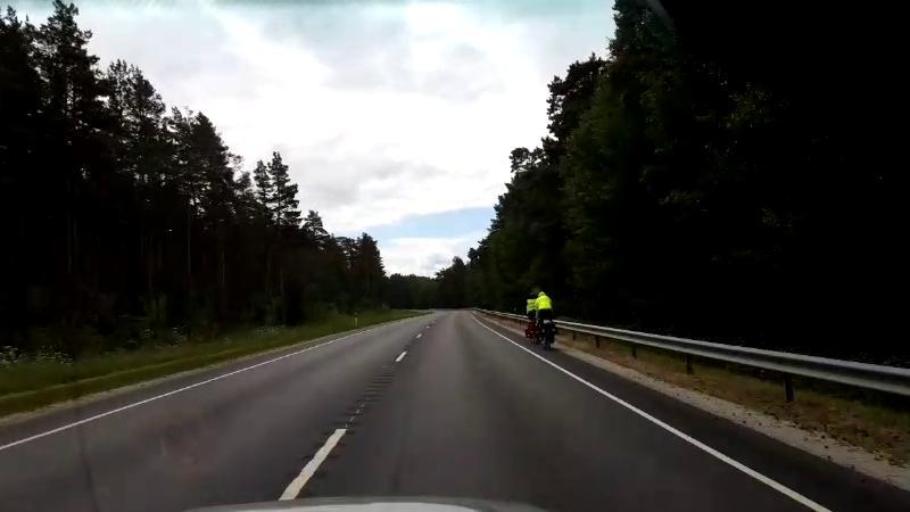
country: EE
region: Paernumaa
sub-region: Paernu linn
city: Parnu
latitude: 58.1524
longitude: 24.4989
